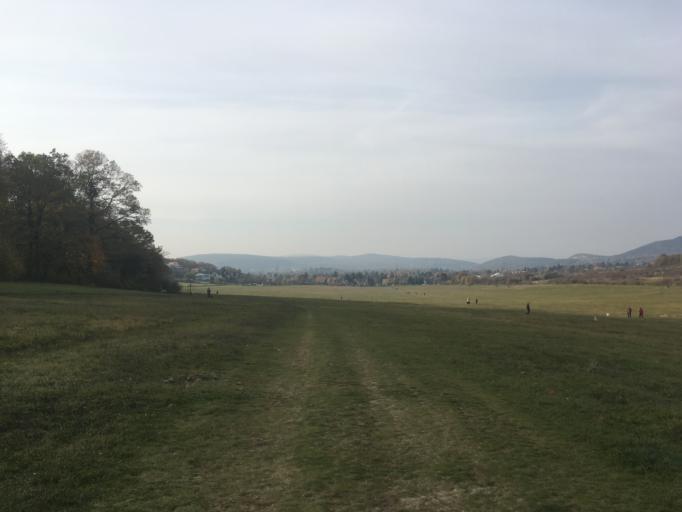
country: HU
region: Pest
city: Pilisborosjeno
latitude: 47.5505
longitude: 18.9776
